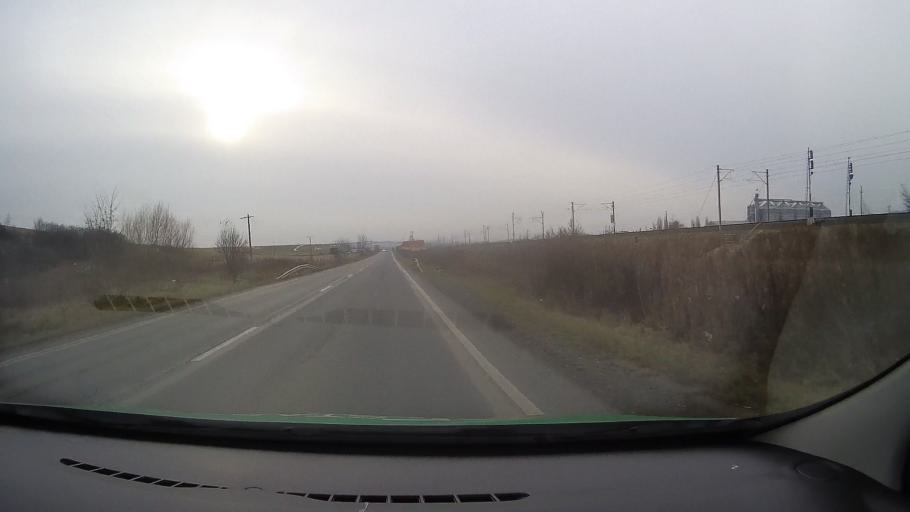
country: RO
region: Hunedoara
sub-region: Municipiul Orastie
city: Orastie
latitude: 45.8686
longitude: 23.2268
